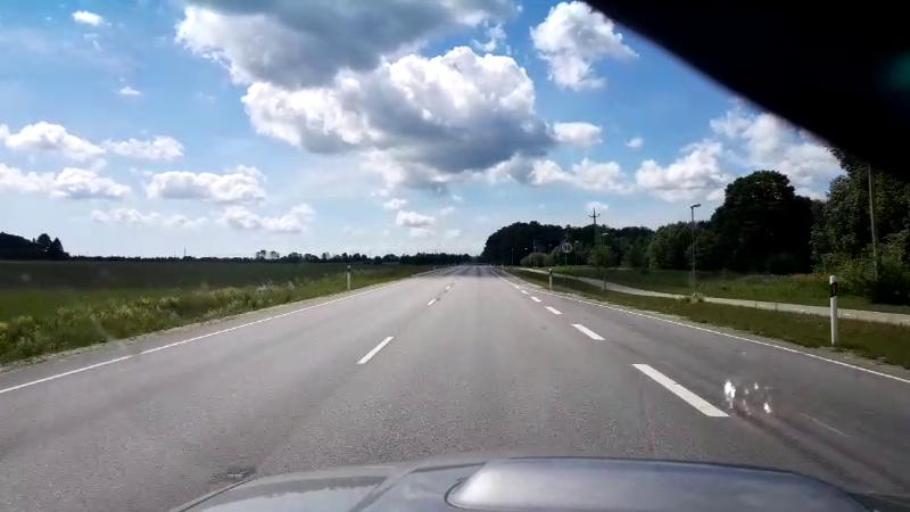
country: EE
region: Jaervamaa
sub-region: Jaerva-Jaani vald
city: Jarva-Jaani
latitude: 59.0207
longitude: 25.7048
